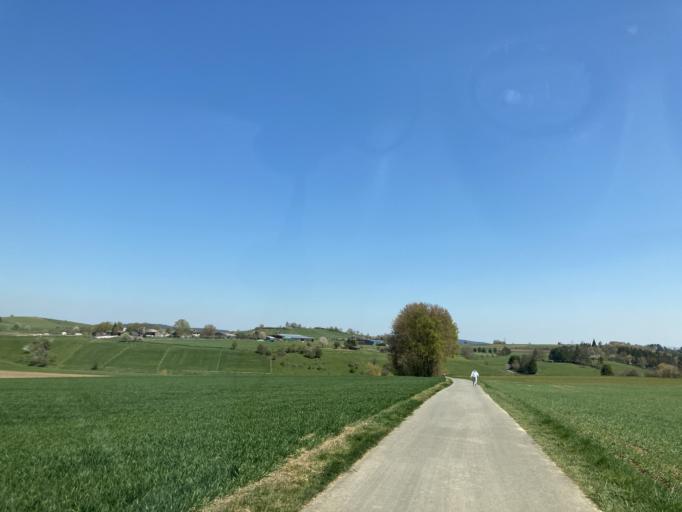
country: DE
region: Baden-Wuerttemberg
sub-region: Tuebingen Region
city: Rottenburg
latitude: 48.4838
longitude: 8.9023
